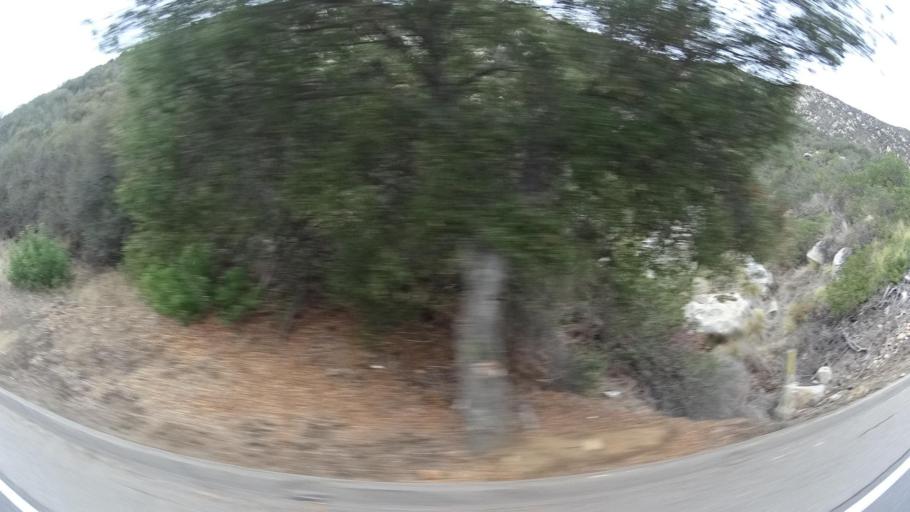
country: US
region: California
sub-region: San Diego County
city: Escondido
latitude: 33.0696
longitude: -117.1221
